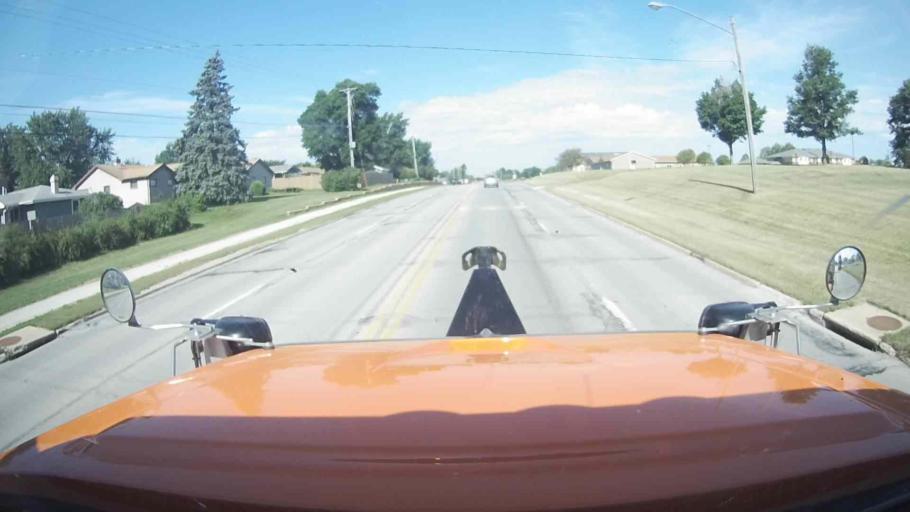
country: US
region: Iowa
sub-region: Union County
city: Creston
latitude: 41.0712
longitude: -94.3761
